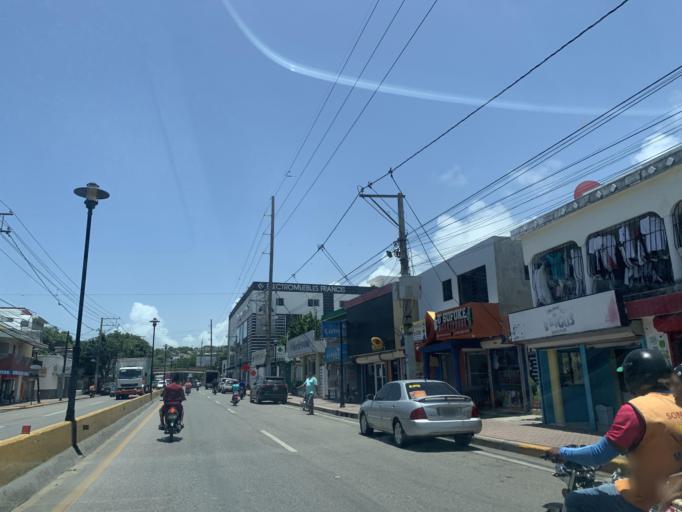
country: DO
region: Puerto Plata
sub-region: Puerto Plata
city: Puerto Plata
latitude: 19.7892
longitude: -70.6986
